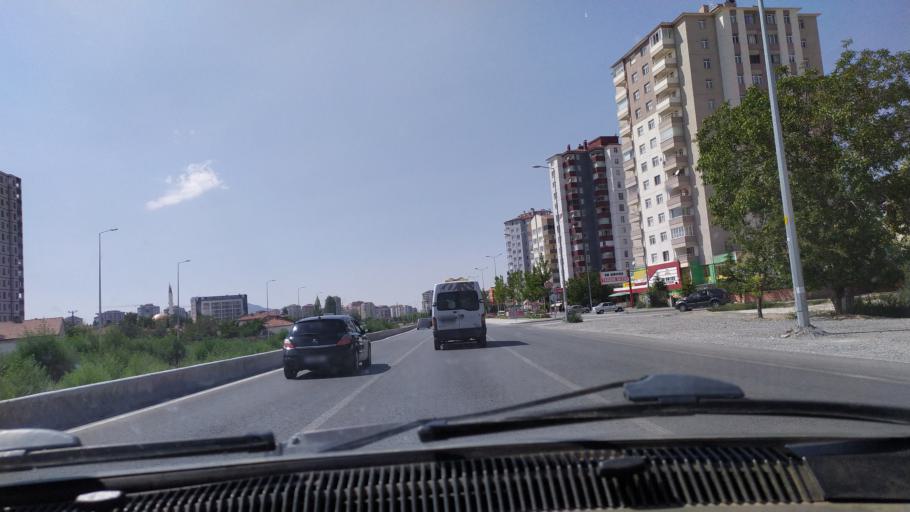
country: TR
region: Kayseri
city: Talas
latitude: 38.7219
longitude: 35.5344
